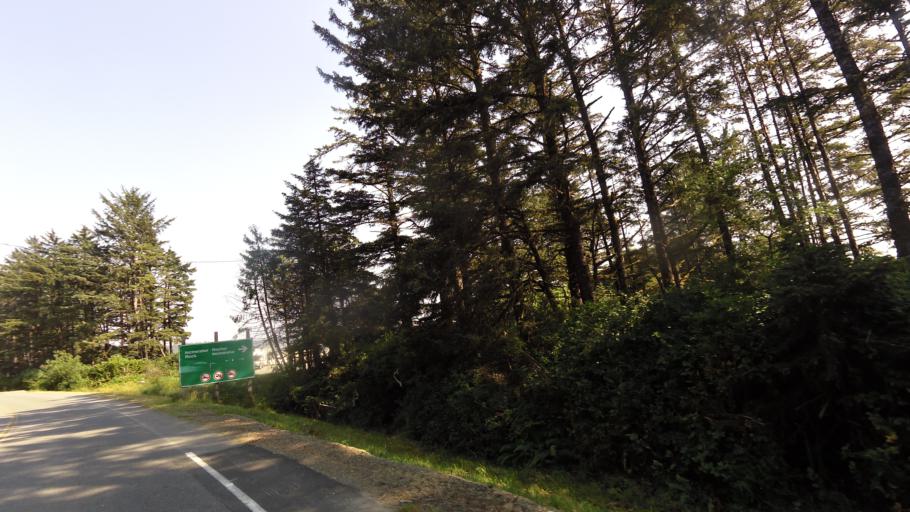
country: CA
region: British Columbia
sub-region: Regional District of Alberni-Clayoquot
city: Tofino
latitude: 49.0729
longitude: -125.7682
